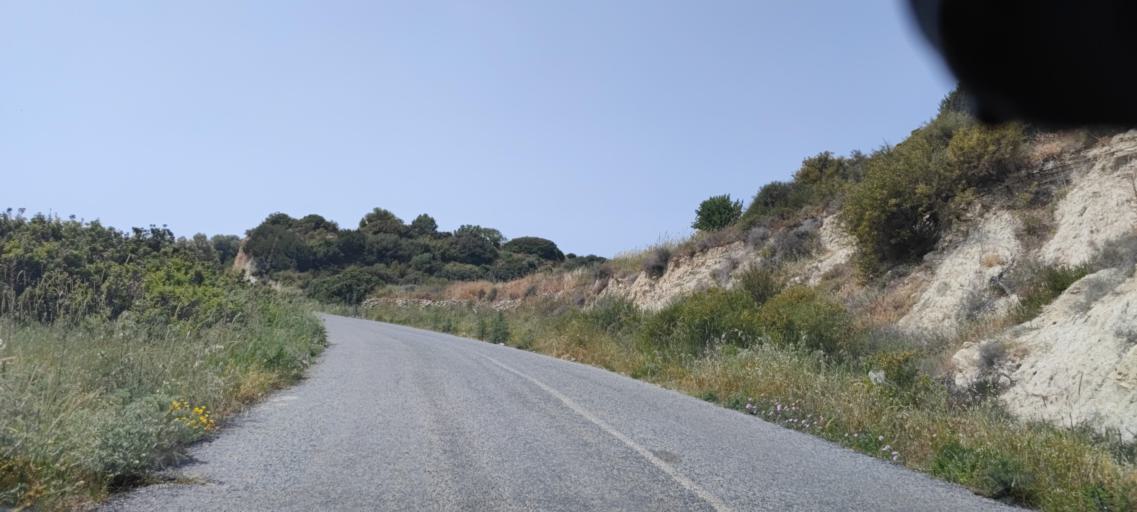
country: CY
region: Ammochostos
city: Rizokarpaso
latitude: 35.5237
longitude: 34.3204
